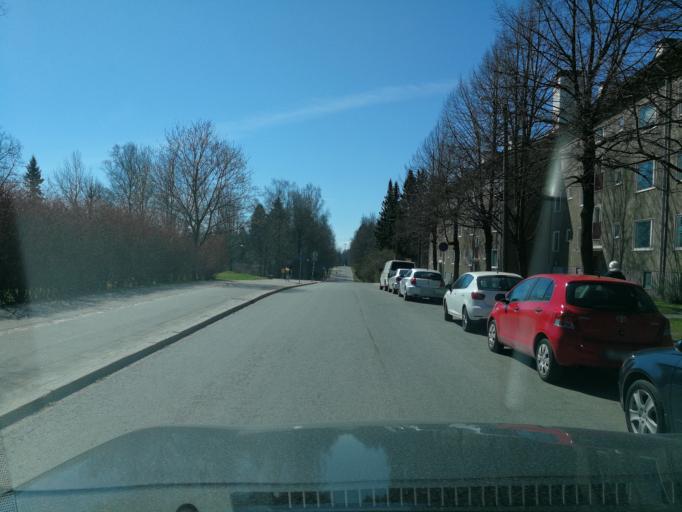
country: FI
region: Uusimaa
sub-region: Helsinki
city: Helsinki
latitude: 60.2280
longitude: 24.9344
